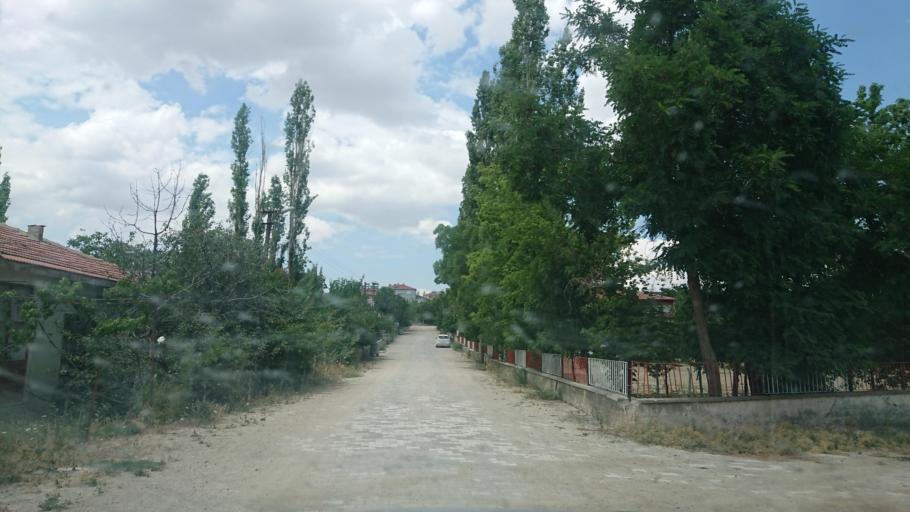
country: TR
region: Aksaray
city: Agacoren
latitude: 38.8715
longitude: 33.9084
